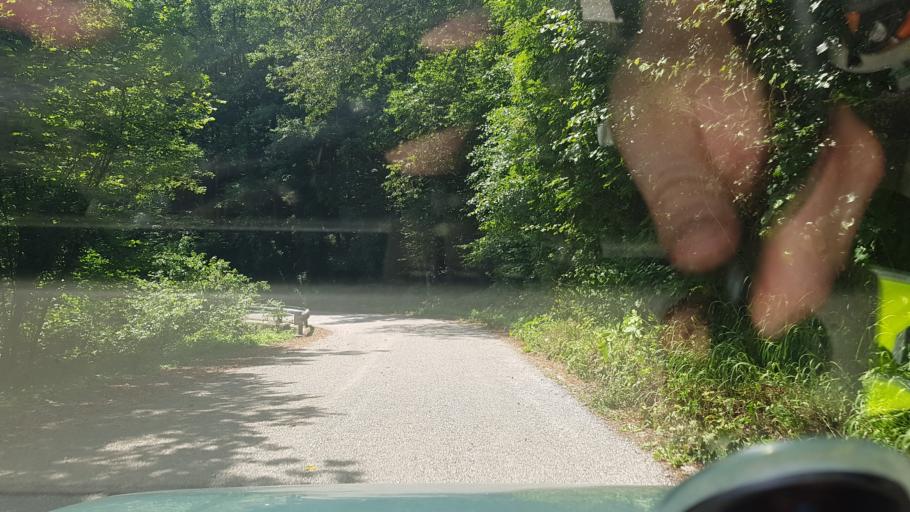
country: IT
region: Friuli Venezia Giulia
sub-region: Provincia di Udine
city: Lusevera
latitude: 46.2758
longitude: 13.2944
